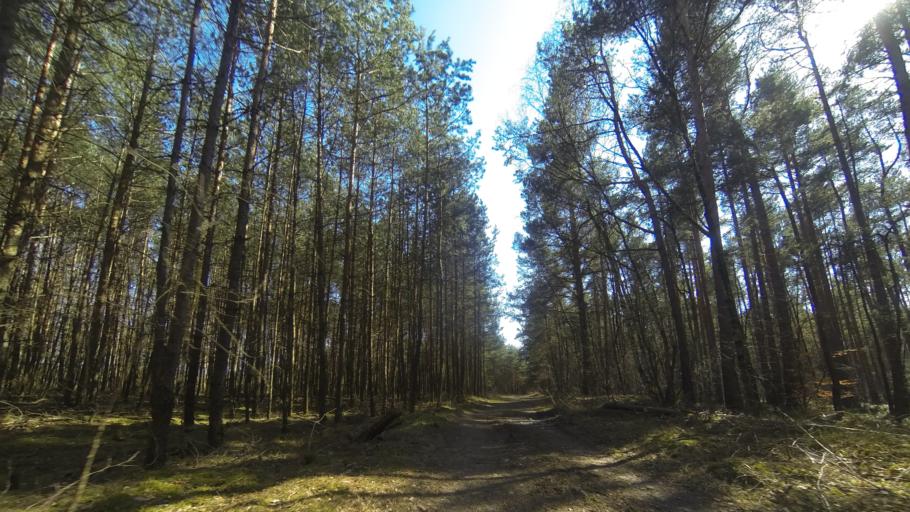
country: DE
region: Saxony
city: Ottendorf-Okrilla
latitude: 51.2060
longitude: 13.8027
